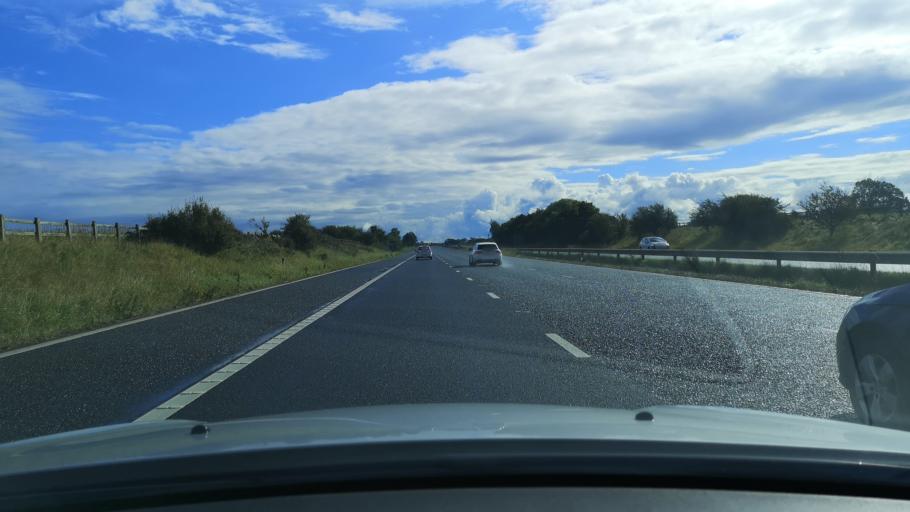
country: GB
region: England
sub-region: East Riding of Yorkshire
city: Pollington
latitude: 53.6914
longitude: -1.1102
